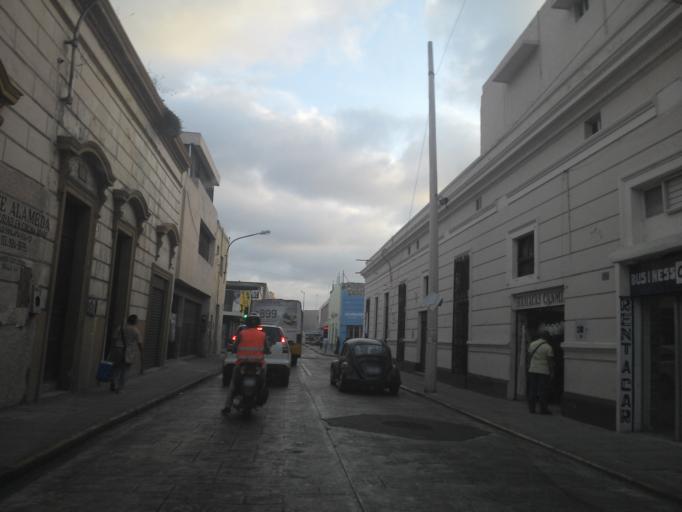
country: MX
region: Yucatan
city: Merida
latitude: 20.9700
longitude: -89.6213
